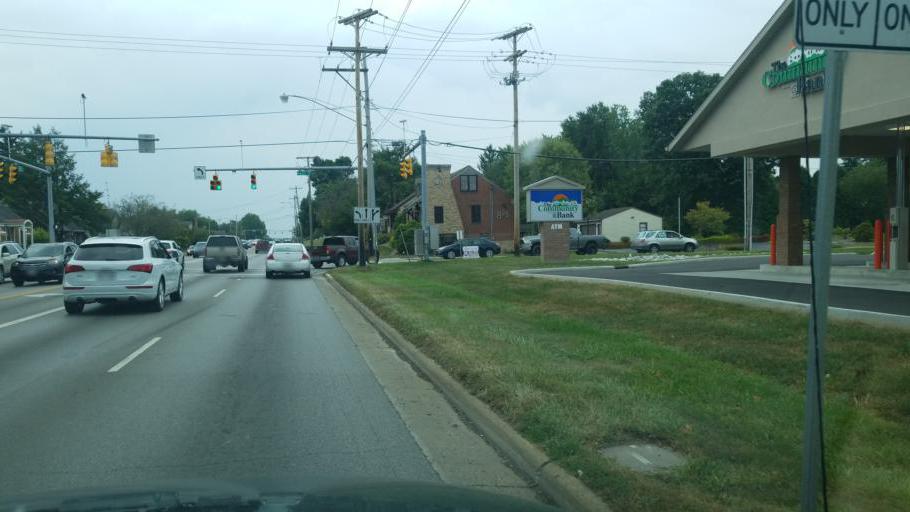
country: US
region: Ohio
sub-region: Licking County
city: Newark
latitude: 40.0713
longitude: -82.4289
